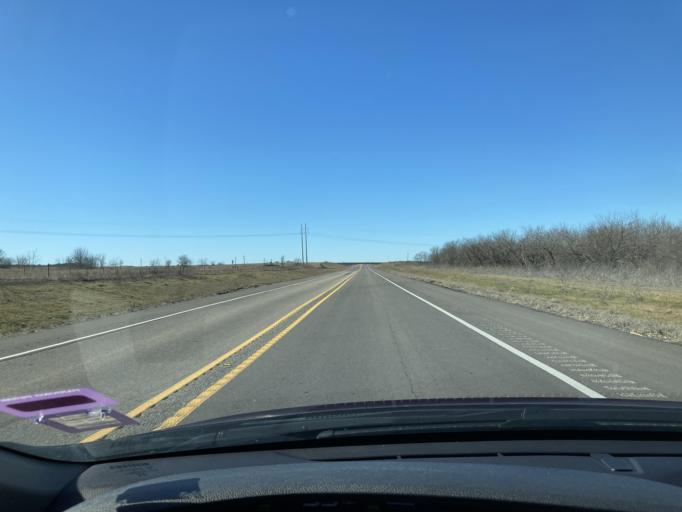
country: US
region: Texas
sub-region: Navarro County
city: Corsicana
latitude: 32.0452
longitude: -96.4327
